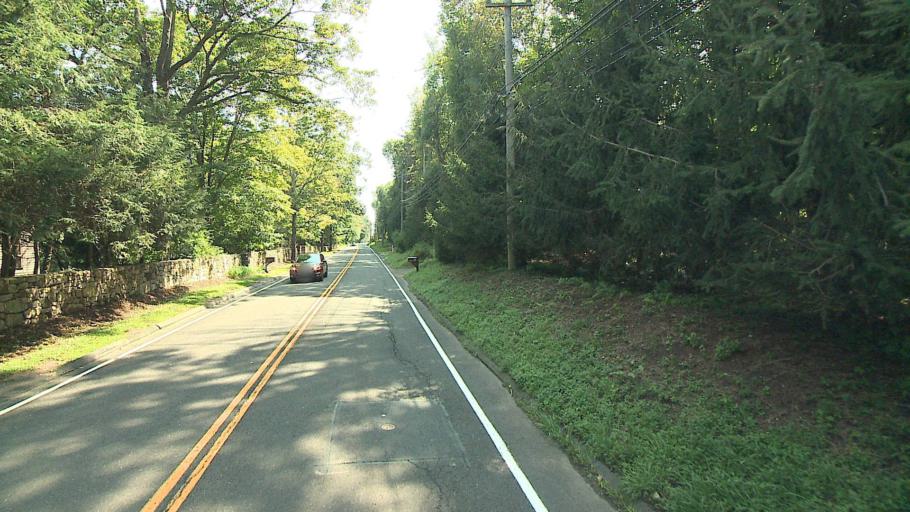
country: US
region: Connecticut
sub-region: Fairfield County
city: Georgetown
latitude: 41.2384
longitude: -73.4084
